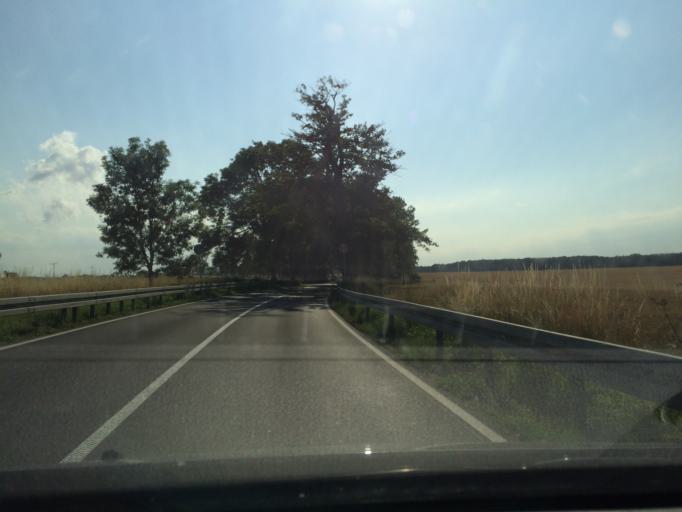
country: DE
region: Mecklenburg-Vorpommern
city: Ostseebad Binz
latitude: 54.4131
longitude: 13.5337
